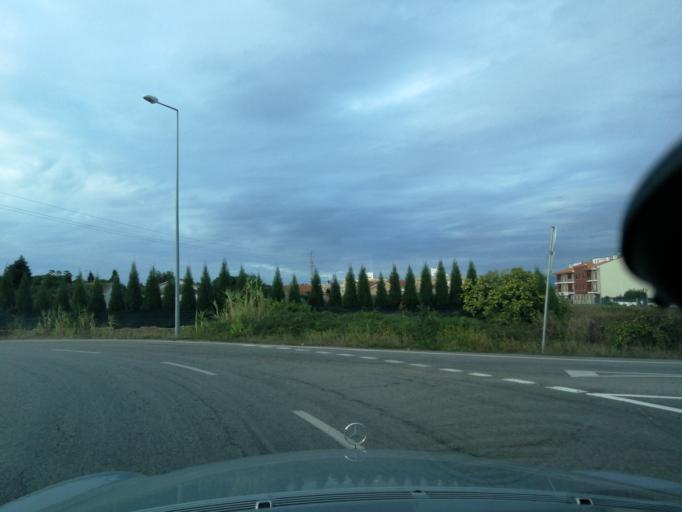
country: PT
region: Aveiro
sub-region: Agueda
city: Valongo
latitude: 40.6088
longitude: -8.4649
